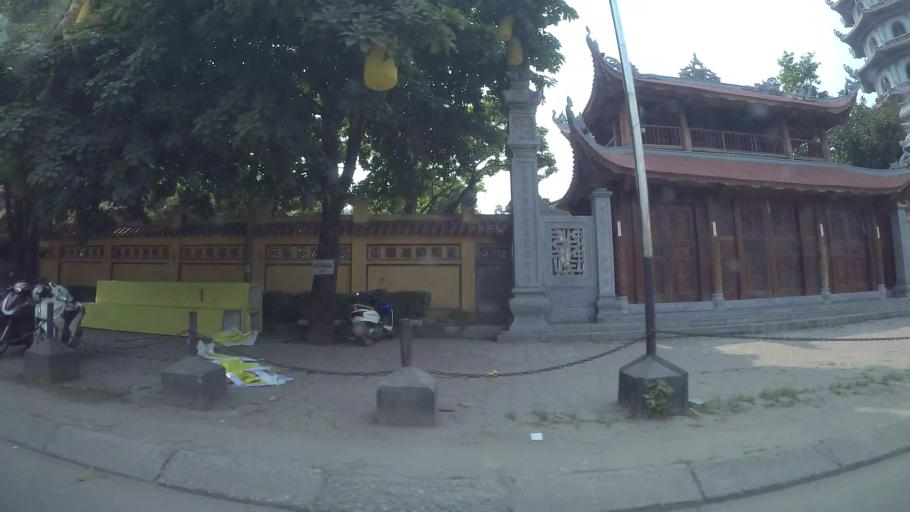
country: VN
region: Ha Noi
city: Van Dien
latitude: 20.9633
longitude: 105.8187
